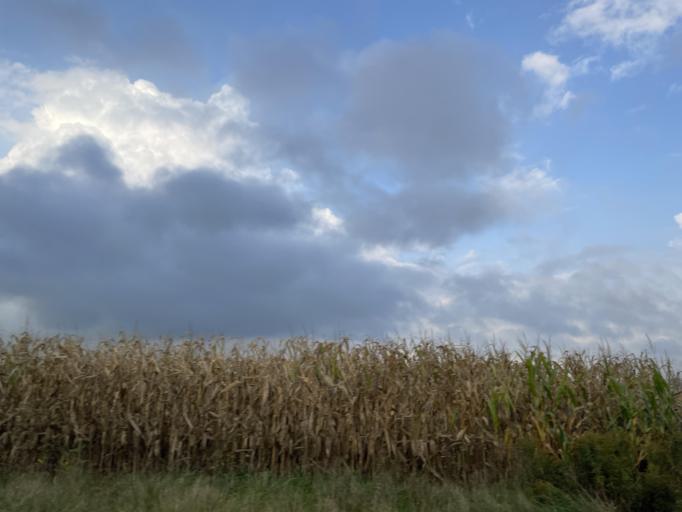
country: CA
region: Ontario
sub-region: Wellington County
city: Guelph
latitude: 43.5006
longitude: -80.2620
